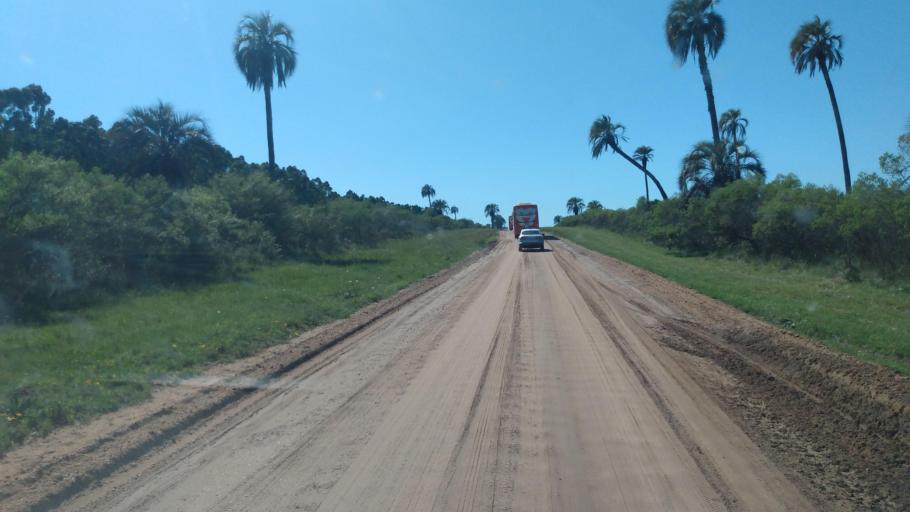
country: AR
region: Entre Rios
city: Ubajay
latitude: -31.8548
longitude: -58.2900
